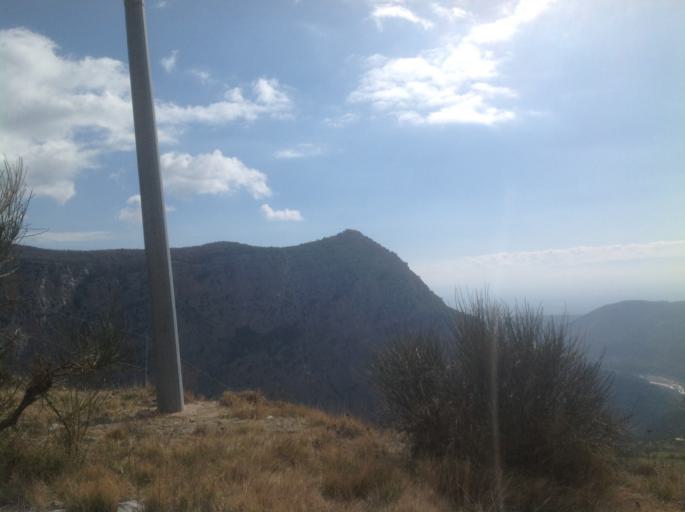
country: IT
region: Calabria
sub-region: Provincia di Cosenza
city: Civita
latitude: 39.8419
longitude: 16.3080
